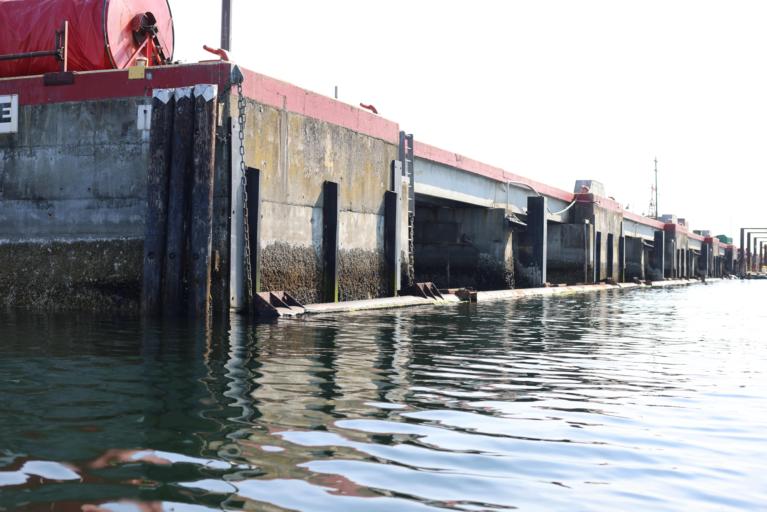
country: CA
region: British Columbia
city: North Saanich
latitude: 48.6533
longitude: -123.4532
